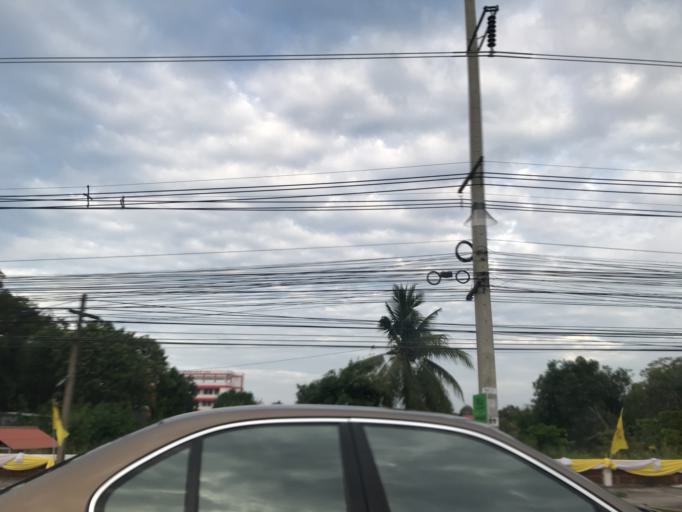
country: TH
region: Chon Buri
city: Bang Lamung
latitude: 13.0238
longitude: 100.9309
